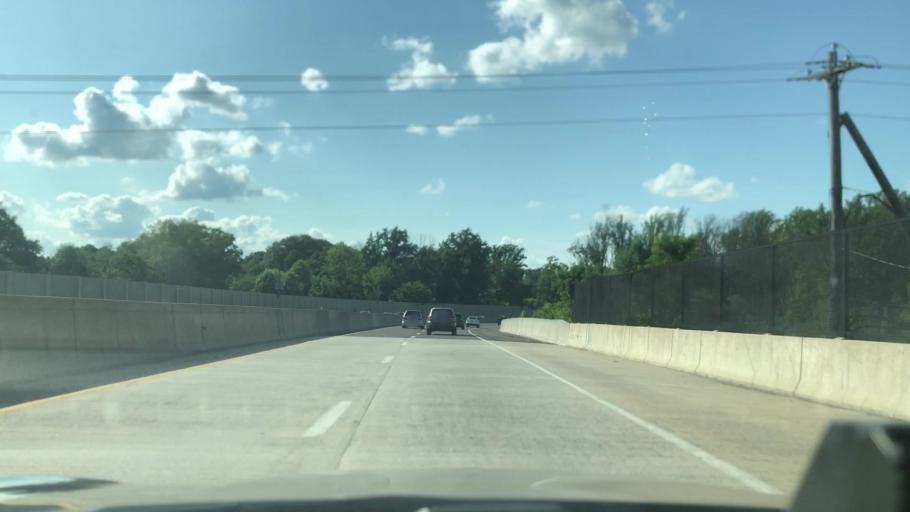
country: US
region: Pennsylvania
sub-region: Montgomery County
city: Spring House
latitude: 40.1728
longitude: -75.2109
